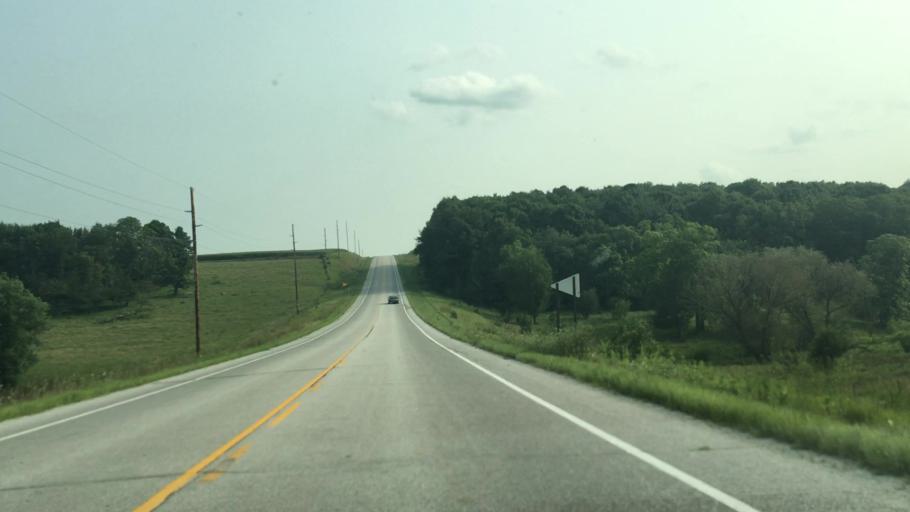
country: US
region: Minnesota
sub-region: Fillmore County
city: Harmony
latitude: 43.5761
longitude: -91.9299
